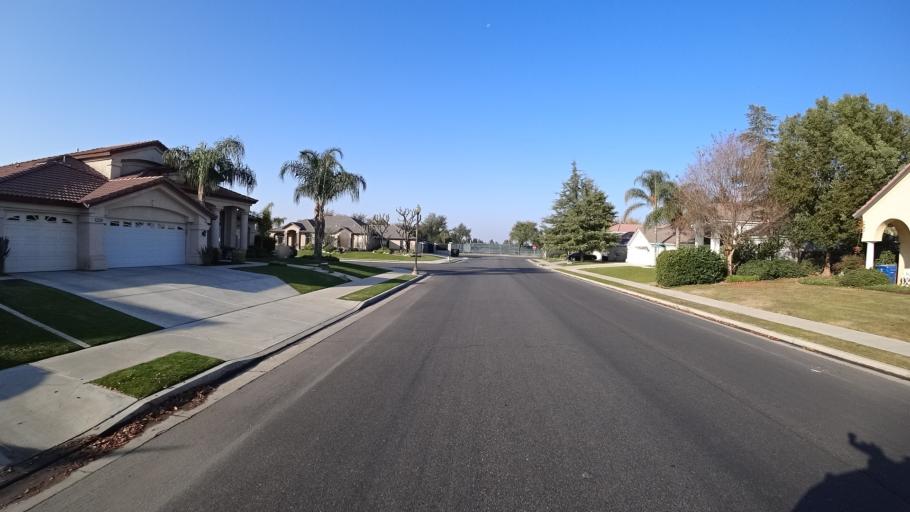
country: US
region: California
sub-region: Kern County
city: Greenacres
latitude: 35.3640
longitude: -119.1269
